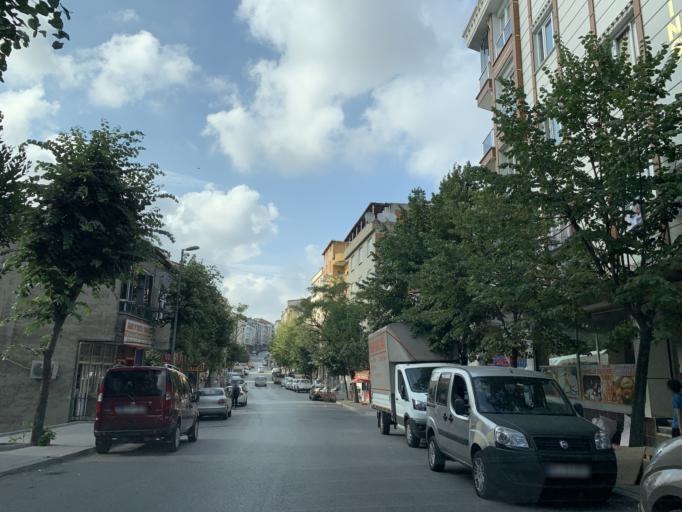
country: TR
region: Istanbul
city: Esenyurt
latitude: 41.0281
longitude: 28.6749
